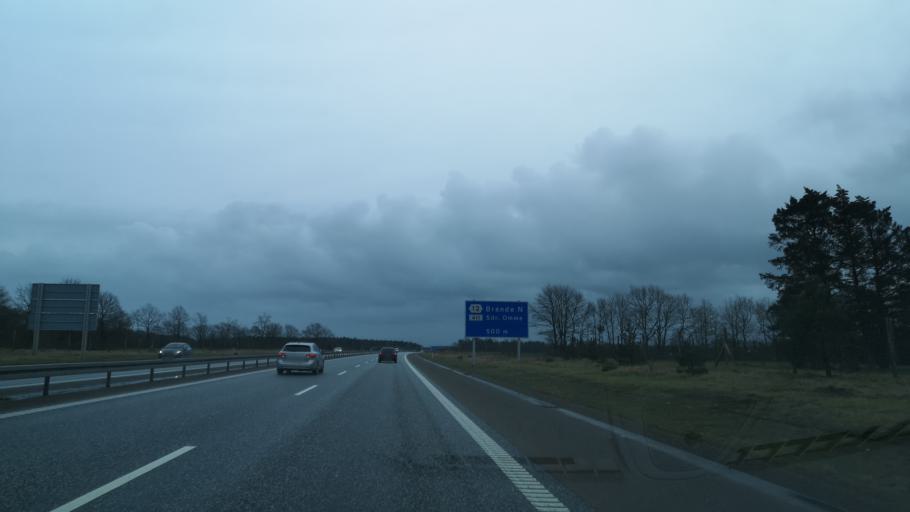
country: DK
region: Central Jutland
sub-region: Ikast-Brande Kommune
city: Brande
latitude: 55.9728
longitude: 9.0862
